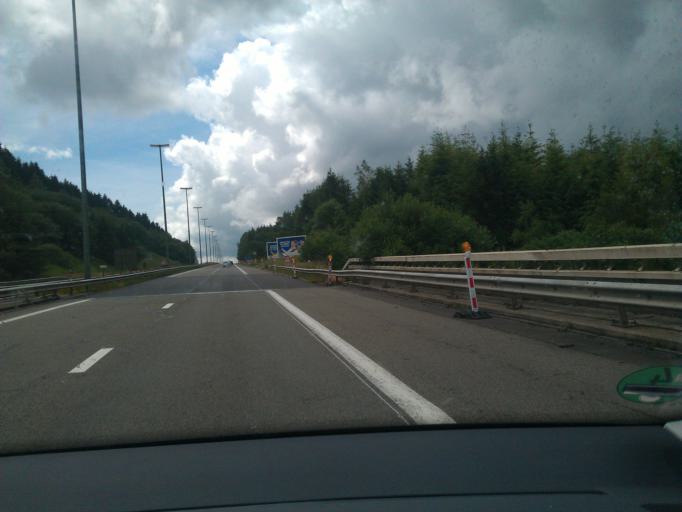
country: BE
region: Wallonia
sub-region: Province de Liege
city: Saint-Vith
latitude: 50.2617
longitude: 6.1459
